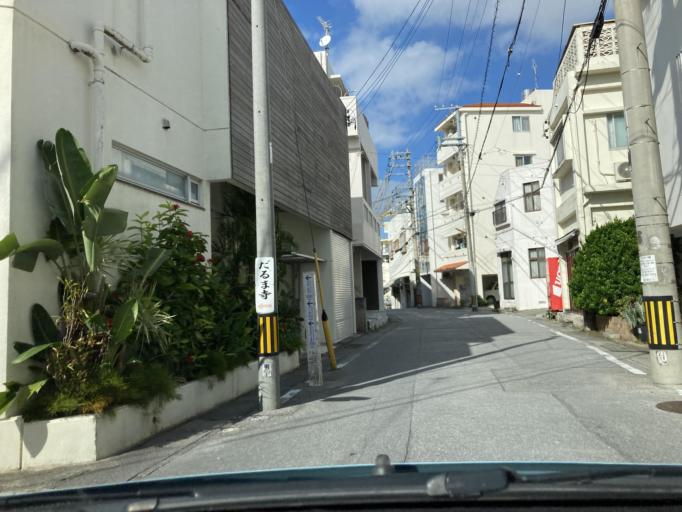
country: JP
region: Okinawa
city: Naha-shi
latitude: 26.2177
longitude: 127.7229
